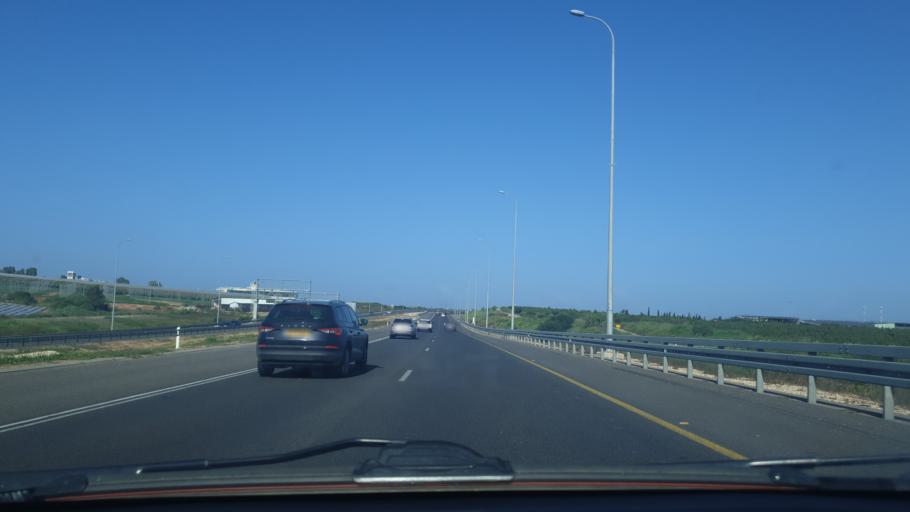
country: IL
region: Tel Aviv
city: Kefar Shemaryahu
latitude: 32.2177
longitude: 34.8374
